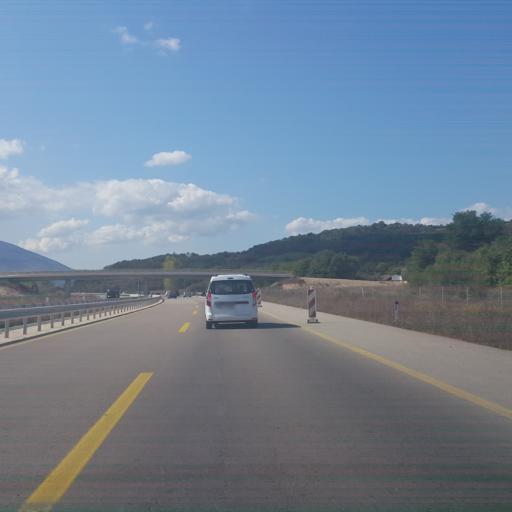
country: RS
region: Central Serbia
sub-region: Pirotski Okrug
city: Bela Palanka
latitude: 43.2355
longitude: 22.3649
